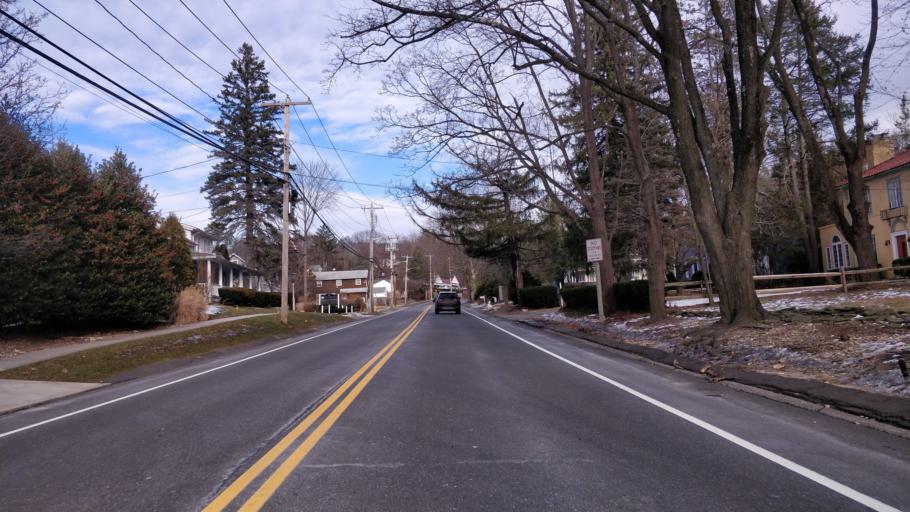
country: US
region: New York
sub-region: Suffolk County
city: Halesite
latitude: 40.8768
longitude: -73.4125
